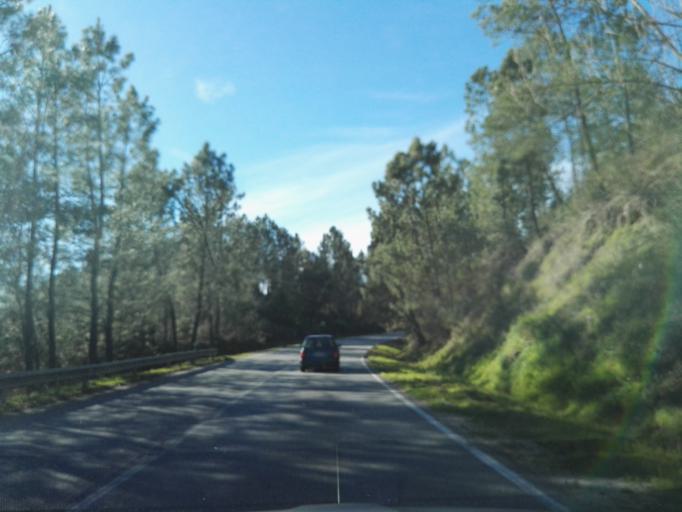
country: PT
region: Santarem
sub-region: Abrantes
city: Alferrarede
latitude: 39.4722
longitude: -8.0693
